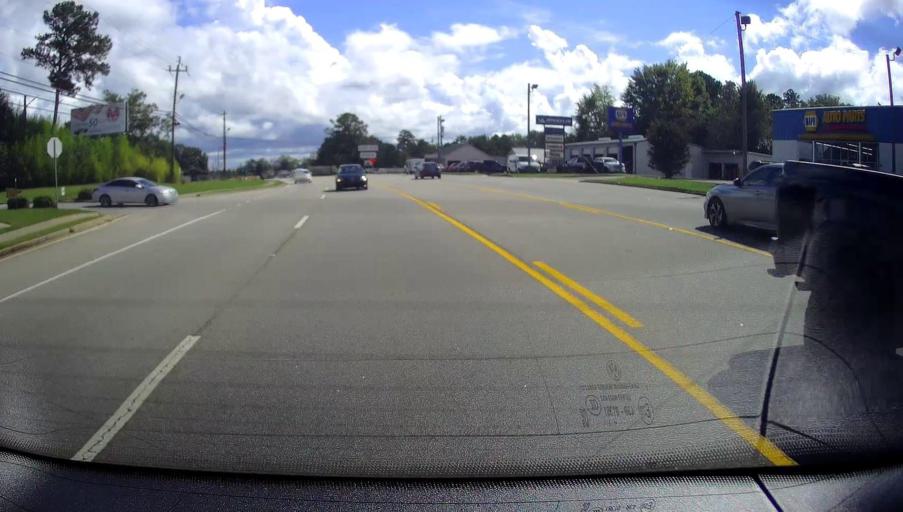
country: US
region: Georgia
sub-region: Baldwin County
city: Milledgeville
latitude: 33.0985
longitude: -83.2454
